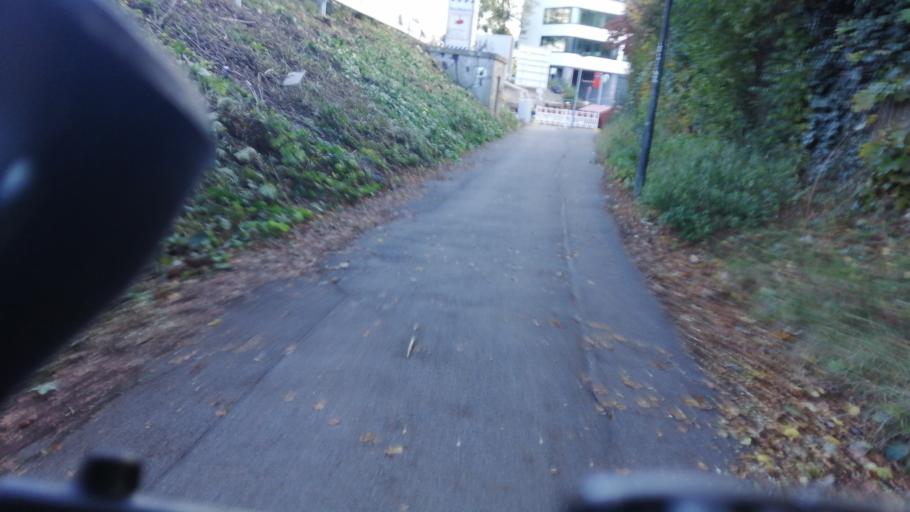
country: DE
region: Bavaria
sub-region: Upper Bavaria
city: Munich
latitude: 48.1192
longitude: 11.5957
